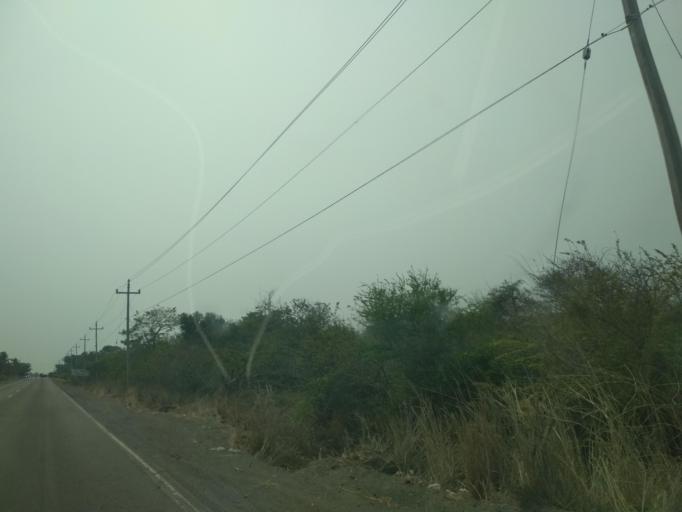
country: MX
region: Veracruz
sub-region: Veracruz
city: Delfino Victoria (Santa Fe)
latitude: 19.1928
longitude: -96.2851
